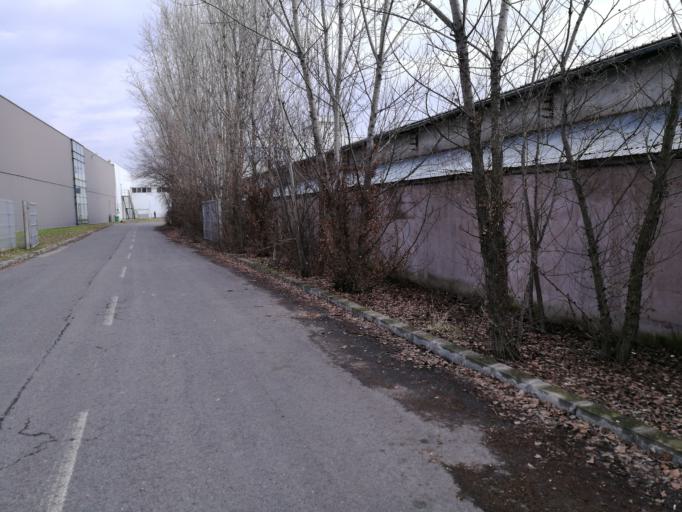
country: RO
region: Ilfov
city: Dobroesti
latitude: 44.4374
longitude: 26.1836
